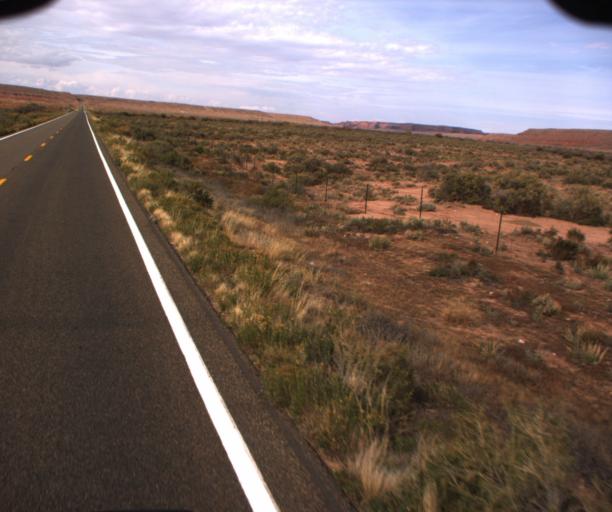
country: US
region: Arizona
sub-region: Apache County
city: Many Farms
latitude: 36.5283
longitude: -109.5032
